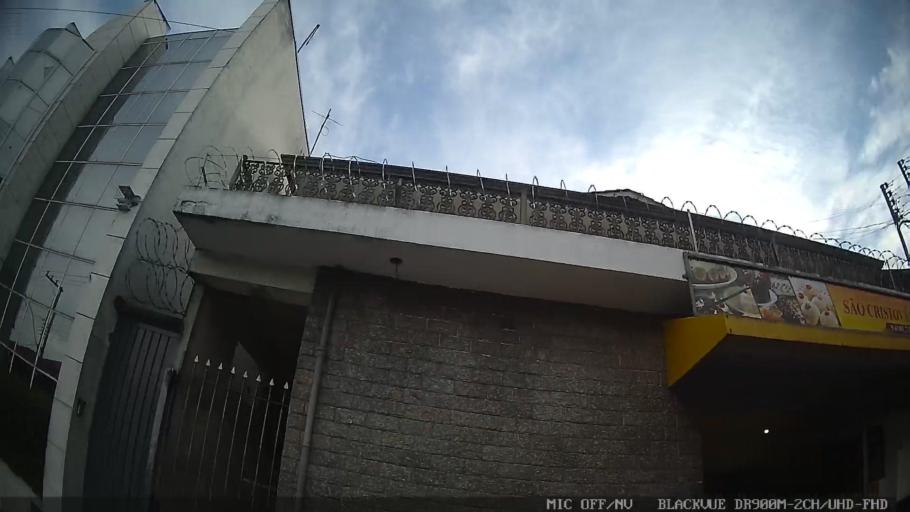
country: BR
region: Sao Paulo
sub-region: Braganca Paulista
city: Braganca Paulista
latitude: -22.9408
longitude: -46.5452
